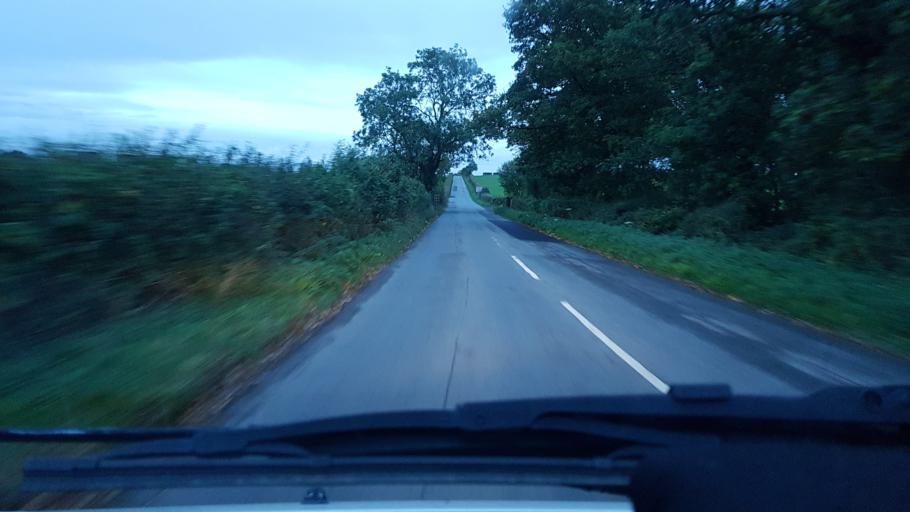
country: GB
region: England
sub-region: Worcestershire
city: Great Malvern
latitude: 52.0671
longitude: -2.2907
